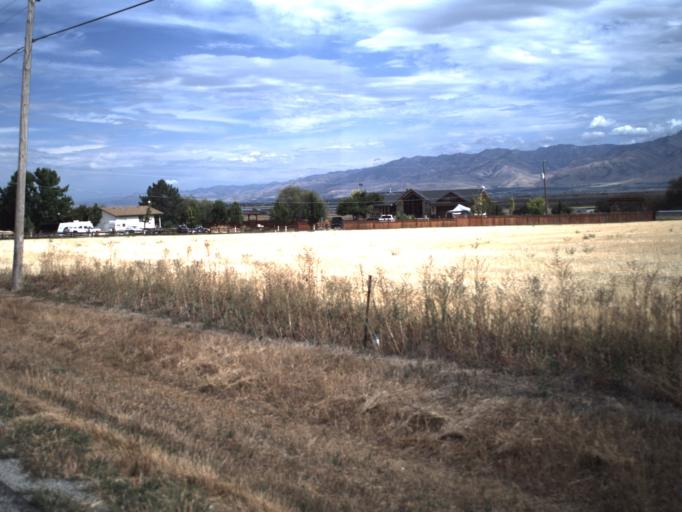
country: US
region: Utah
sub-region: Cache County
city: Mendon
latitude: 41.7275
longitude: -111.9791
